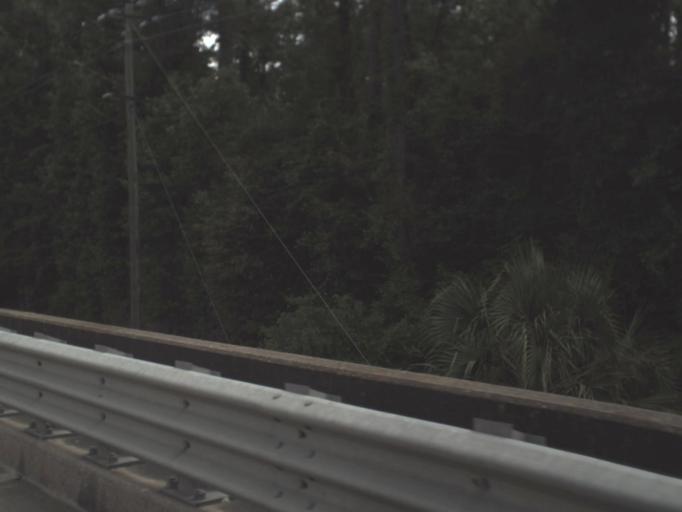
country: US
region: Georgia
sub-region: Charlton County
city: Folkston
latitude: 30.7770
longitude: -81.9788
